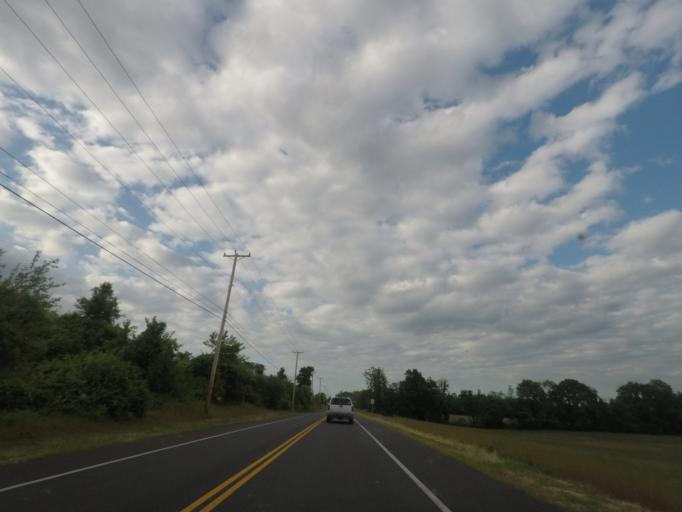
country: US
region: New York
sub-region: Ulster County
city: New Paltz
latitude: 41.7334
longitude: -74.0721
